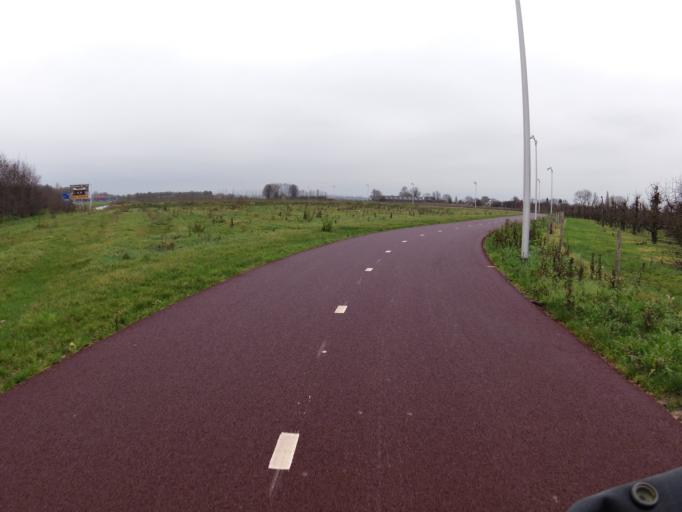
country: NL
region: Gelderland
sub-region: Gemeente Overbetuwe
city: Elst
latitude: 51.9075
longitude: 5.8741
